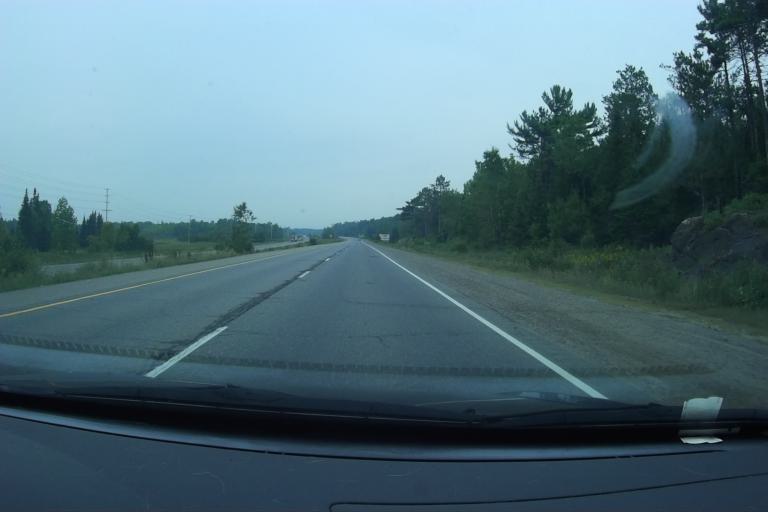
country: CA
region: Ontario
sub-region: Nipissing District
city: North Bay
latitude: 46.2806
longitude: -79.4052
